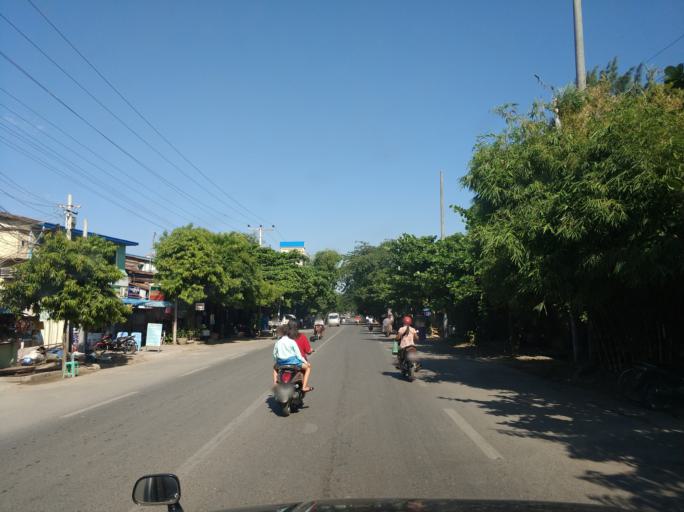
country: MM
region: Mandalay
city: Mandalay
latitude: 21.9707
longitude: 96.0643
